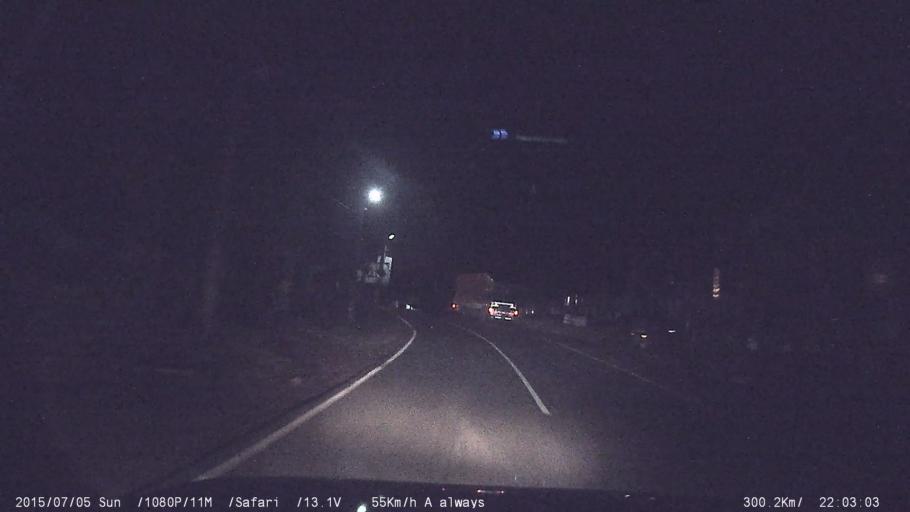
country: IN
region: Kerala
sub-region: Palakkad district
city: Mannarakkat
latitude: 10.9332
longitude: 76.5274
